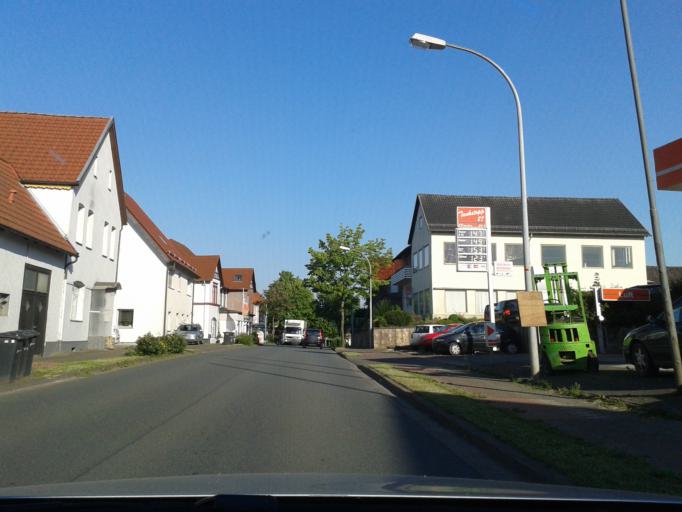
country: DE
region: North Rhine-Westphalia
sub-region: Regierungsbezirk Detmold
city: Dorentrup
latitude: 52.0267
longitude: 9.0565
